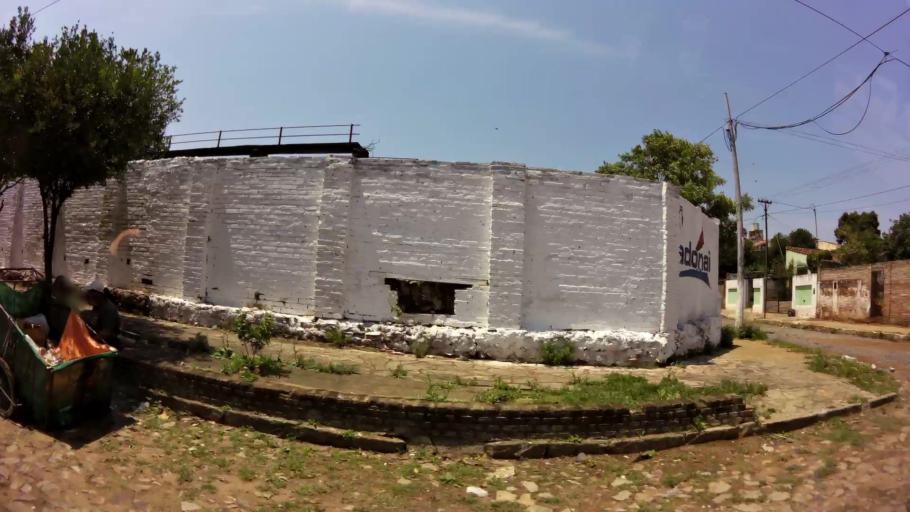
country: PY
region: Asuncion
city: Asuncion
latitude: -25.2964
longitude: -57.6485
